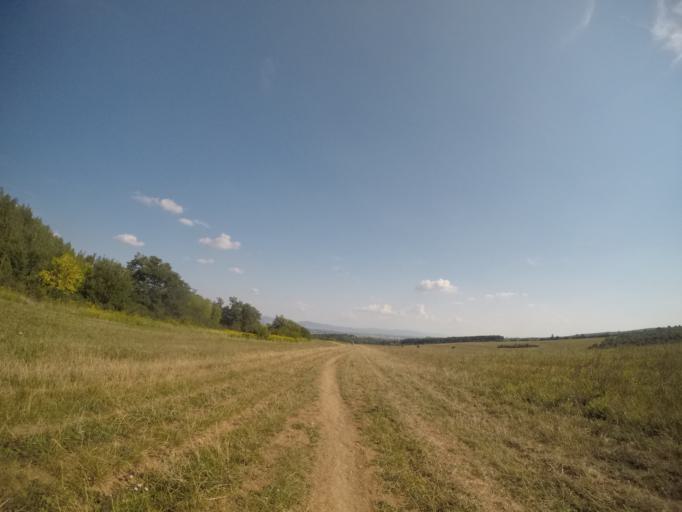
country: SK
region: Kosicky
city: Kosice
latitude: 48.7342
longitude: 21.2124
